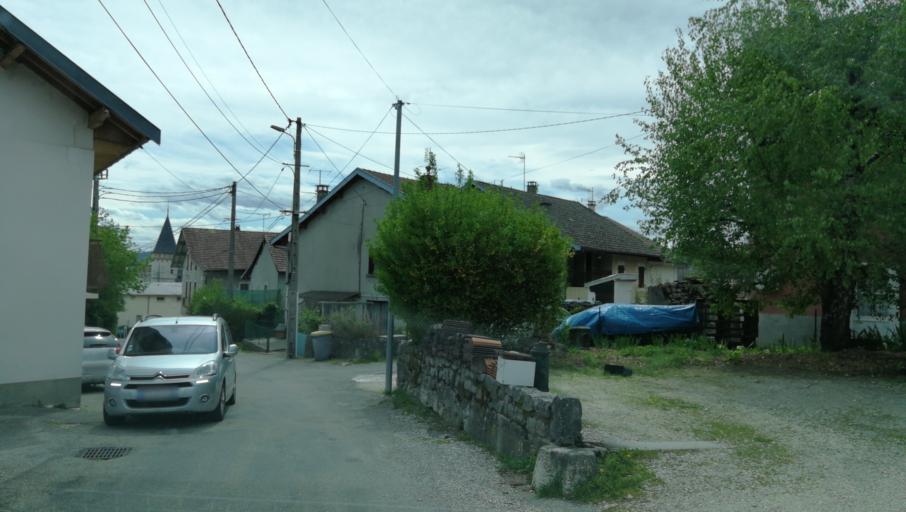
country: FR
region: Rhone-Alpes
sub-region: Departement de l'Ain
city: Bellegarde-sur-Valserine
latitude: 46.0066
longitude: 5.7848
